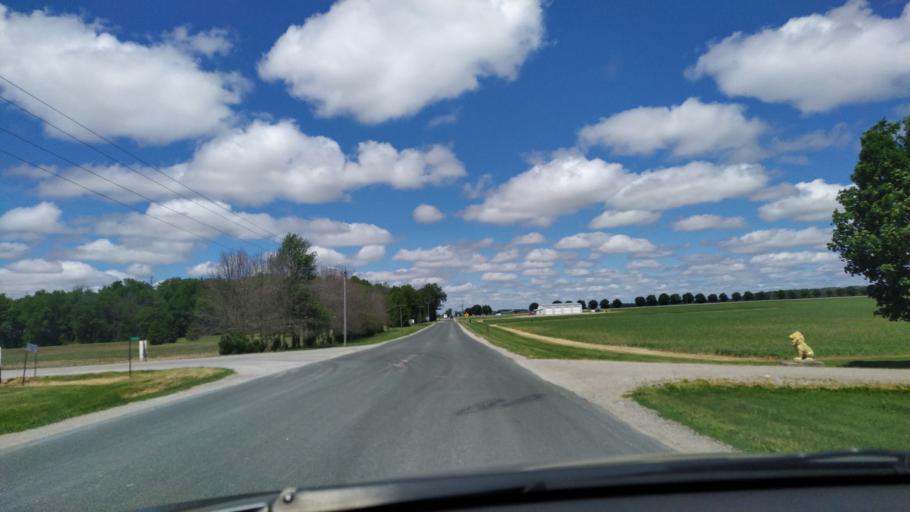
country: CA
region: Ontario
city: Huron East
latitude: 43.4548
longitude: -81.1795
